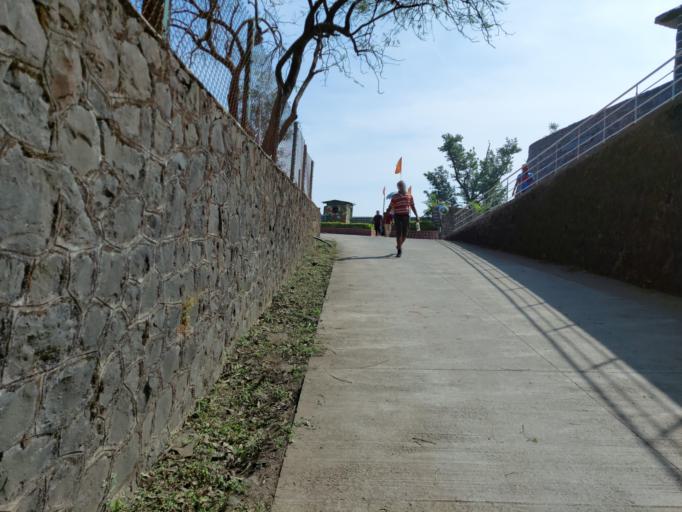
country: IN
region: Maharashtra
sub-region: Pune Division
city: Sasvad
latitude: 18.2811
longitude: 73.9838
